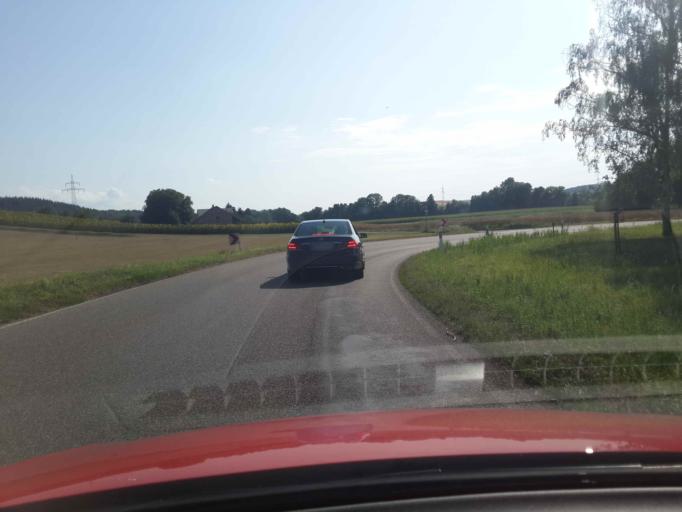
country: DE
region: Baden-Wuerttemberg
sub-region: Regierungsbezirk Stuttgart
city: Gemmingen
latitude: 49.1297
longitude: 9.0133
